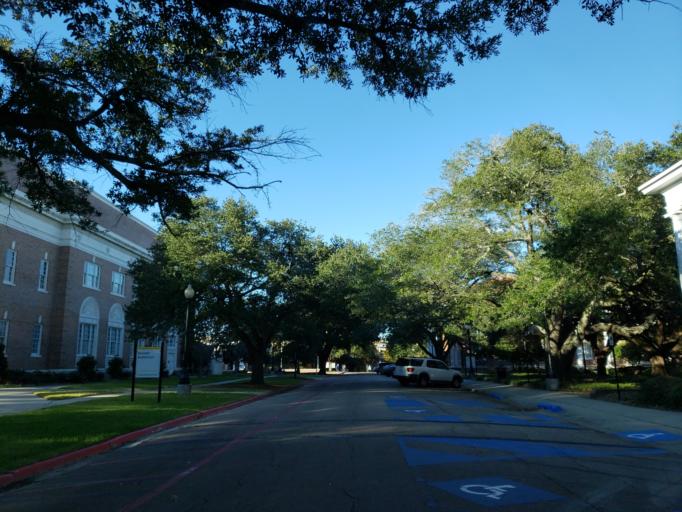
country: US
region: Mississippi
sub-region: Lamar County
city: Arnold Line
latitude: 31.3269
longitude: -89.3323
